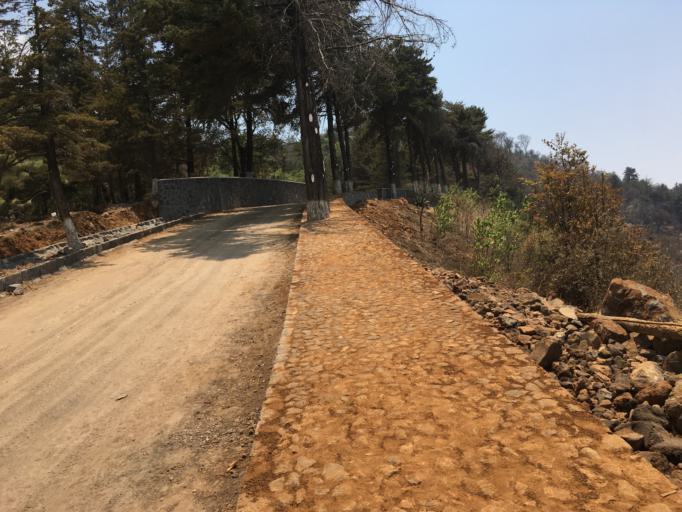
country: MX
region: Michoacan
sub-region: Patzcuaro
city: Santa Ana Chapitiro
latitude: 19.5148
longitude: -101.6364
